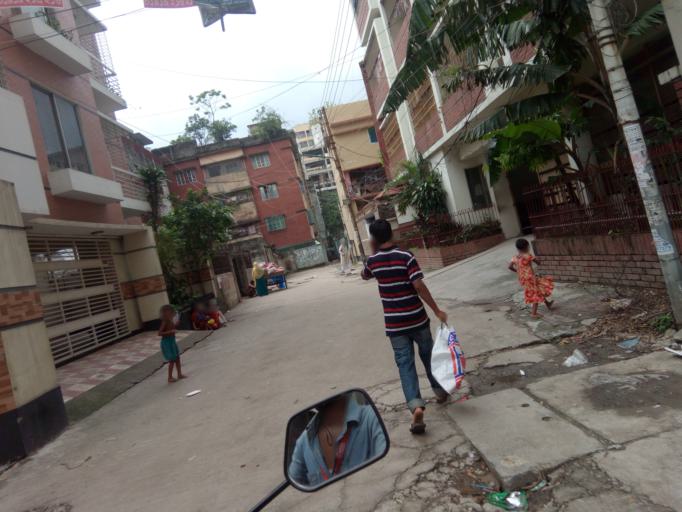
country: BD
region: Dhaka
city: Azimpur
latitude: 23.7612
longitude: 90.3669
